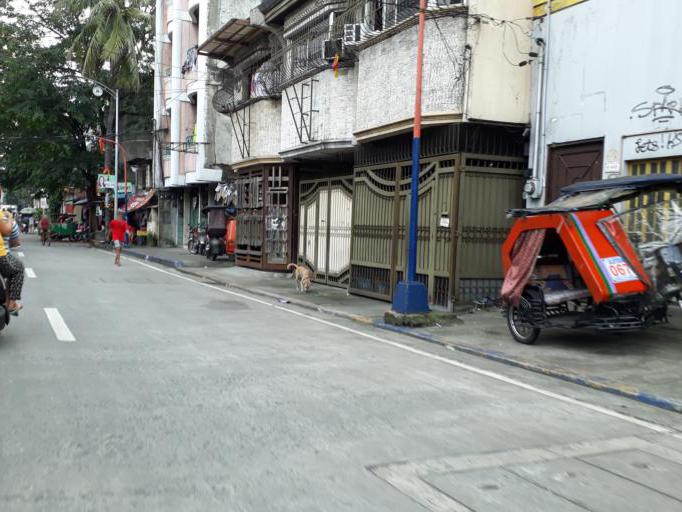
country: PH
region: Metro Manila
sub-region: City of Manila
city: Manila
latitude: 14.6070
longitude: 120.9997
